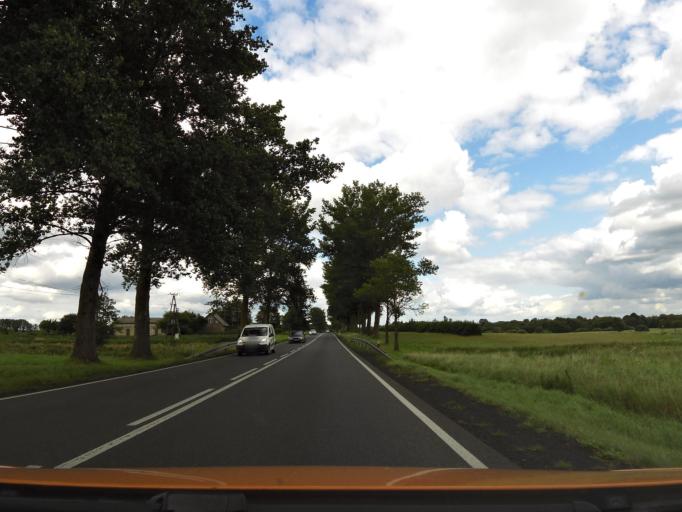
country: PL
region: West Pomeranian Voivodeship
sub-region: Powiat gryficki
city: Ploty
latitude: 53.8526
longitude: 15.3318
